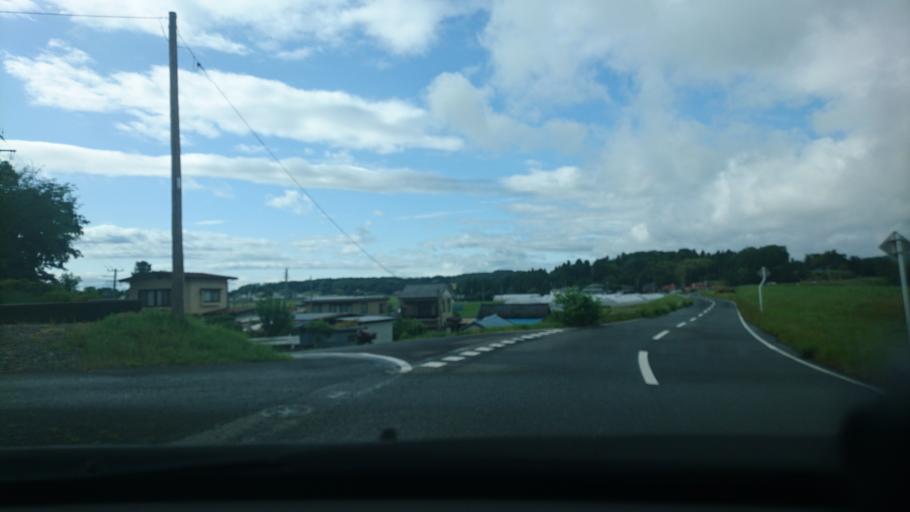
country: JP
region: Miyagi
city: Wakuya
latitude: 38.6859
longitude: 141.2835
